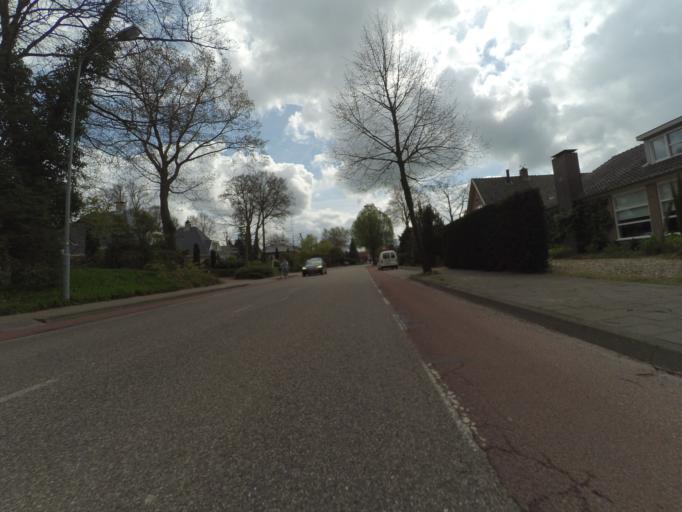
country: NL
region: Gelderland
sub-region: Gemeente Ede
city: Lunteren
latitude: 52.0919
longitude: 5.6181
